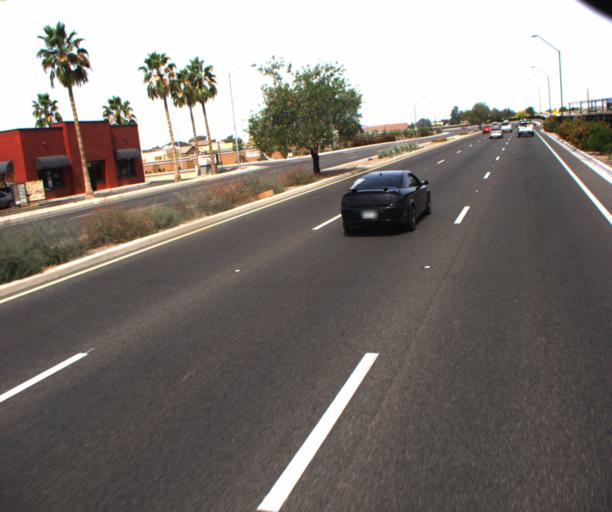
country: US
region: Arizona
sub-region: Maricopa County
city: Peoria
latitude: 33.5889
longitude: -112.2463
